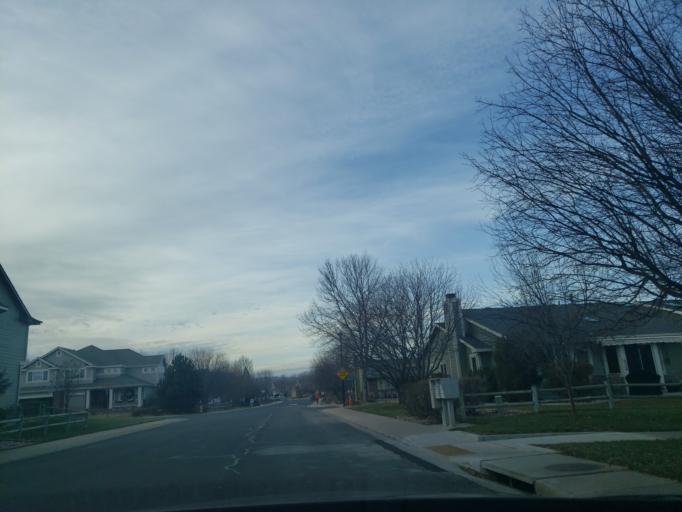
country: US
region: Colorado
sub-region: Larimer County
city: Fort Collins
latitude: 40.5092
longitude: -105.0429
